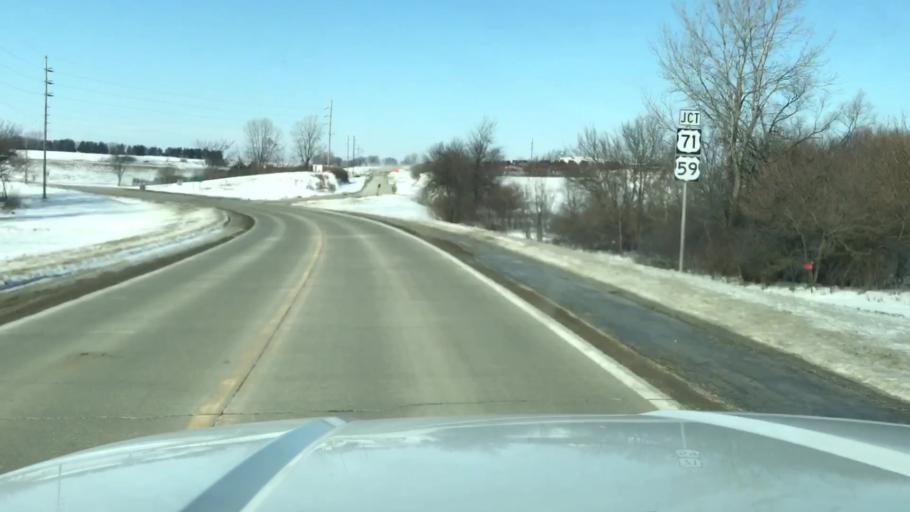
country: US
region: Missouri
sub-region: Andrew County
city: Savannah
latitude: 39.9614
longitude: -94.8572
